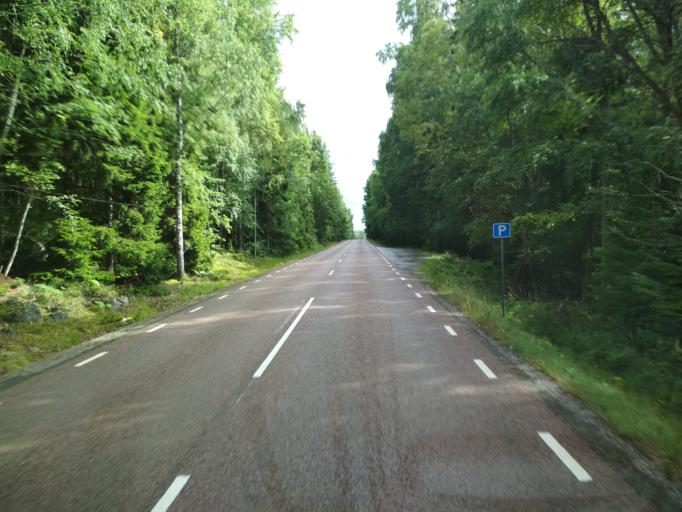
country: SE
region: Vaestmanland
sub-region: Surahammars Kommun
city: Ramnas
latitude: 59.8626
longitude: 16.0878
